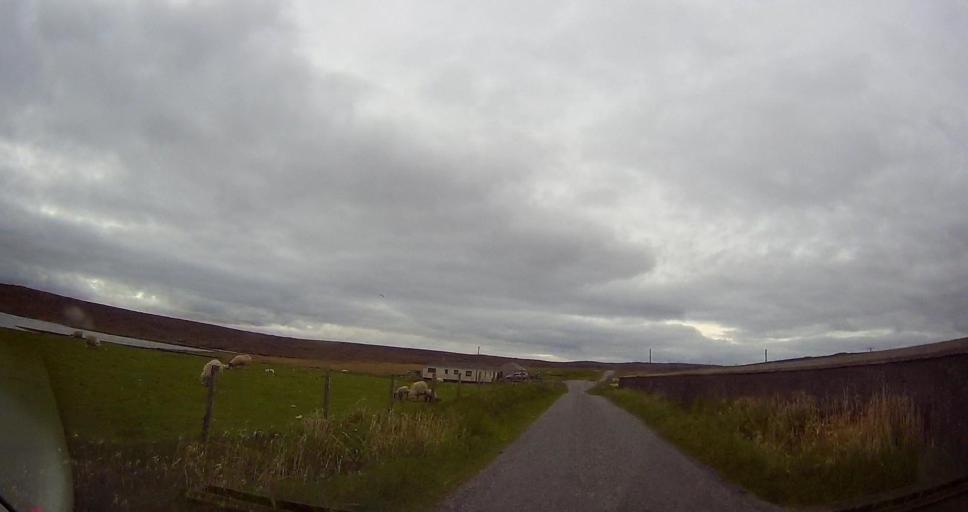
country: GB
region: Scotland
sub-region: Shetland Islands
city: Shetland
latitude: 60.5041
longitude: -1.1019
